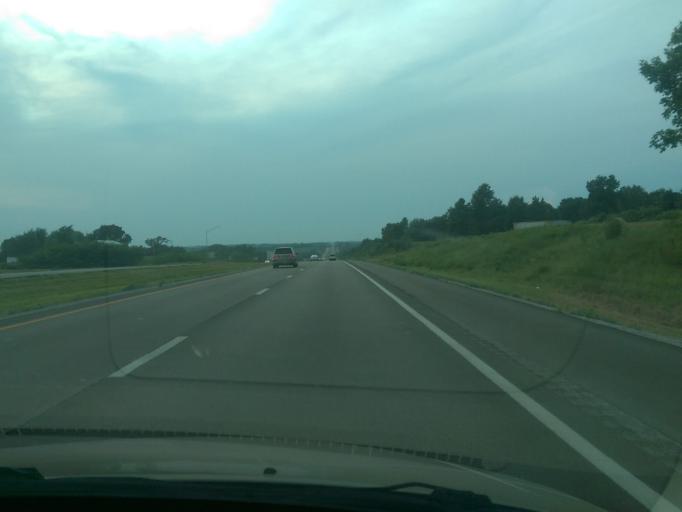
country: US
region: Missouri
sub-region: Andrew County
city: Country Club Village
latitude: 39.8589
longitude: -94.8116
